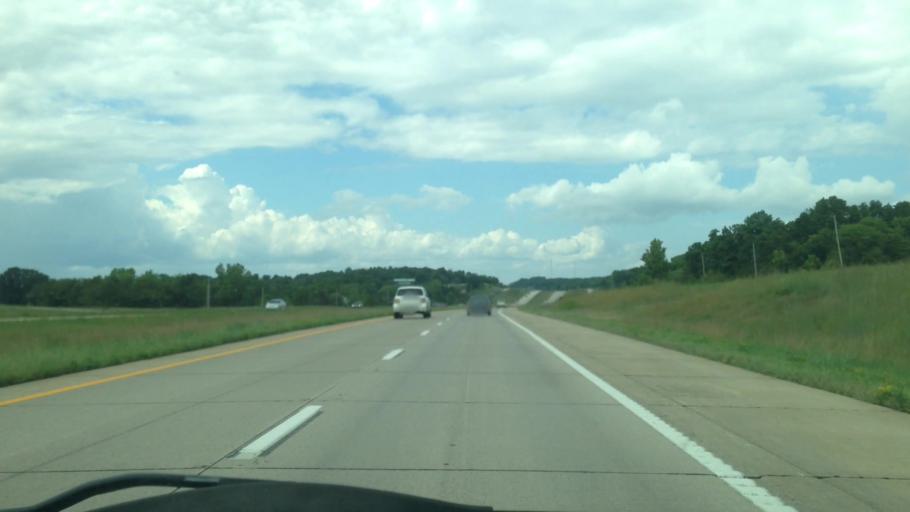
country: US
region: Missouri
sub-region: Pike County
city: Bowling Green
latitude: 39.4146
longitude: -91.2500
